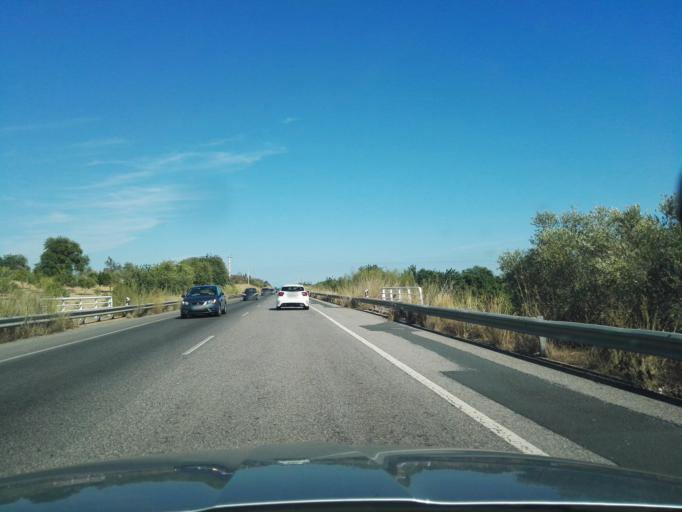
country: PT
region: Faro
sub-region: Tavira
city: Tavira
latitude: 37.1259
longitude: -7.6778
